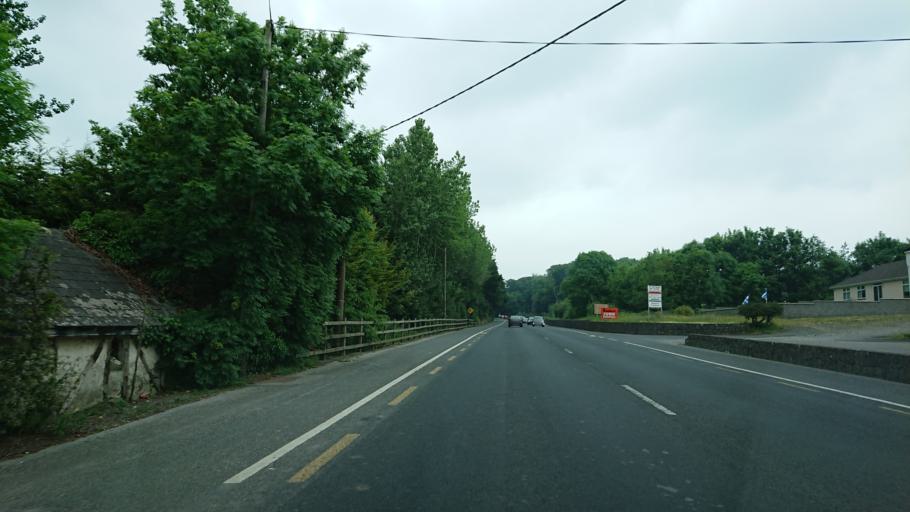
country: IE
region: Munster
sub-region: Waterford
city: Waterford
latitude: 52.2065
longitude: -7.1162
